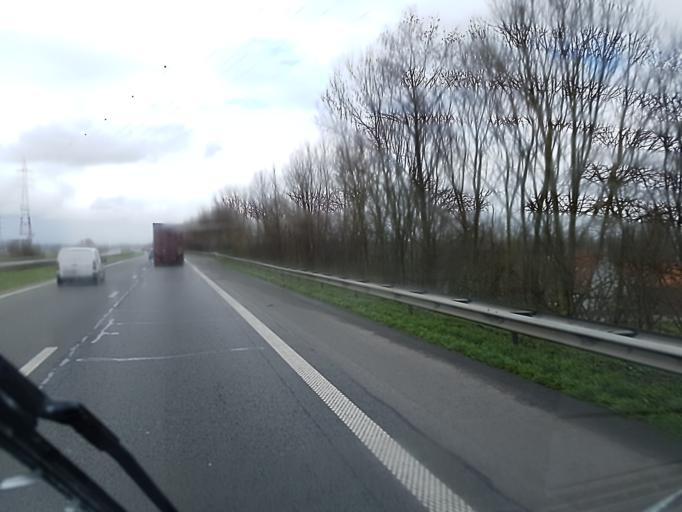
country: BE
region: Wallonia
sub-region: Province du Hainaut
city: Estaimpuis
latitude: 50.6800
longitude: 3.2913
